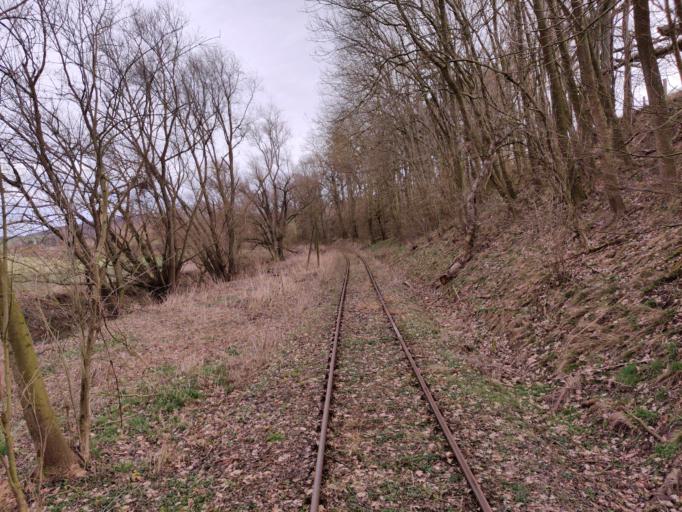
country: DE
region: Lower Saxony
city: Bockenem
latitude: 52.0455
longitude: 10.1250
